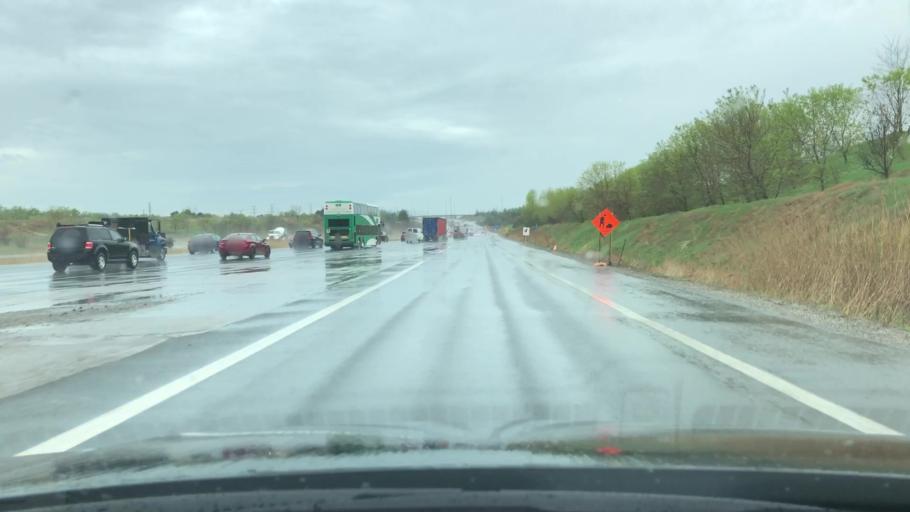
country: CA
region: Ontario
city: Markham
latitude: 43.8696
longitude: -79.2387
